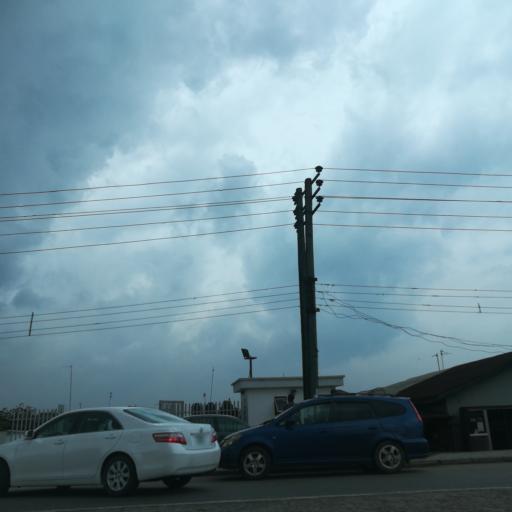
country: NG
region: Rivers
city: Port Harcourt
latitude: 4.8247
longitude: 7.0390
